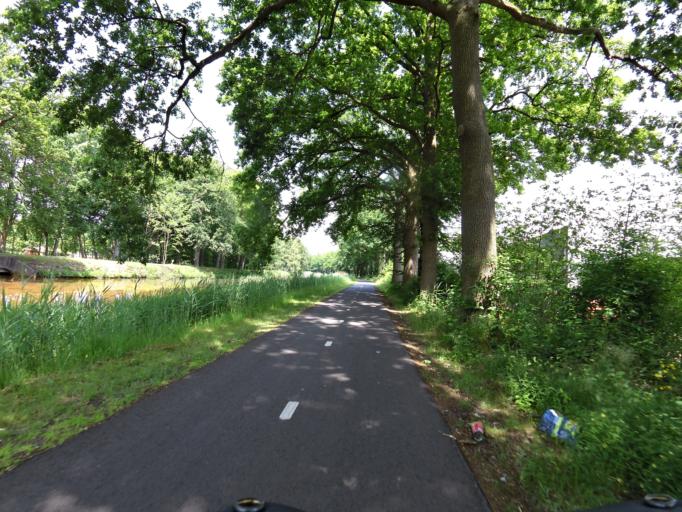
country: NL
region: Gelderland
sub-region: Gemeente Apeldoorn
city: Loenen
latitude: 52.1432
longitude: 6.0409
